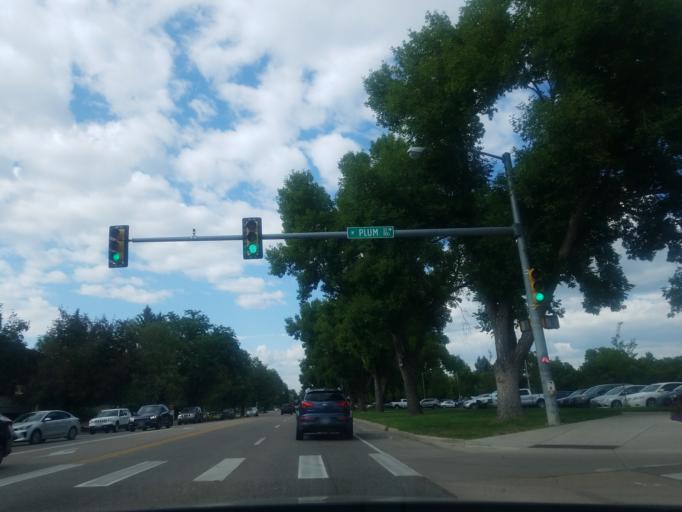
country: US
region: Colorado
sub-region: Larimer County
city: Fort Collins
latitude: 40.5765
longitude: -105.0959
